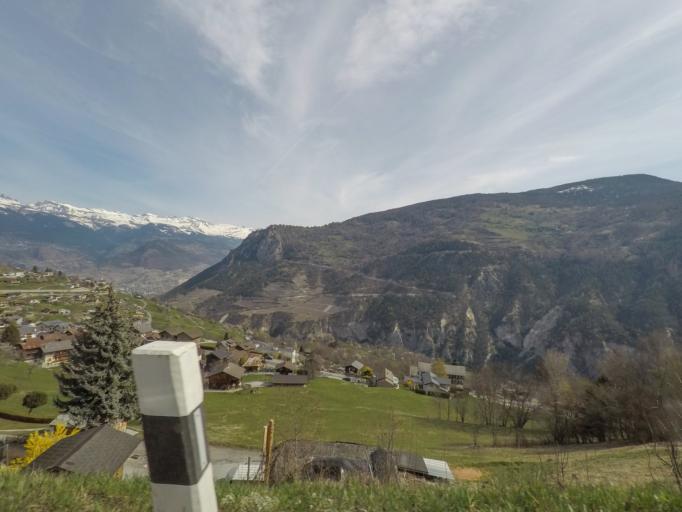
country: CH
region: Valais
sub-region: Herens District
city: Vex
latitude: 46.2067
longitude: 7.3991
